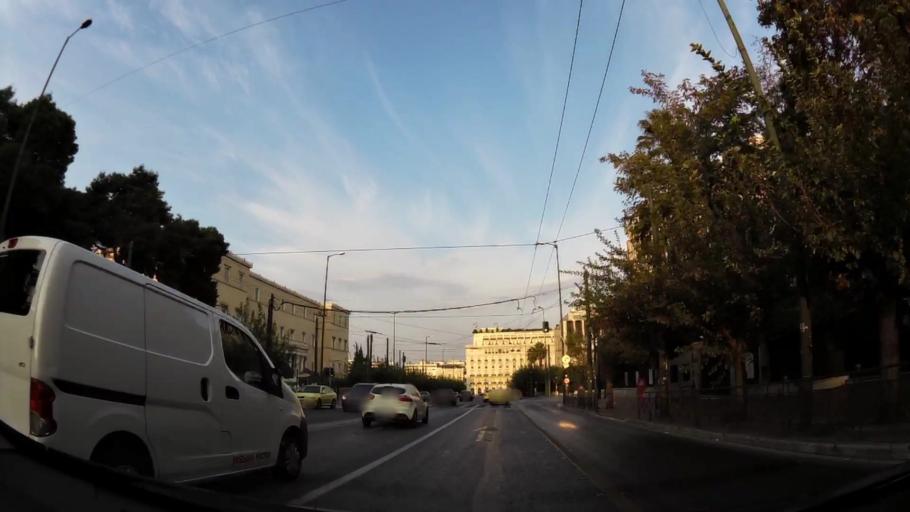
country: GR
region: Attica
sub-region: Nomarchia Athinas
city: Vyronas
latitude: 37.9760
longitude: 23.7381
